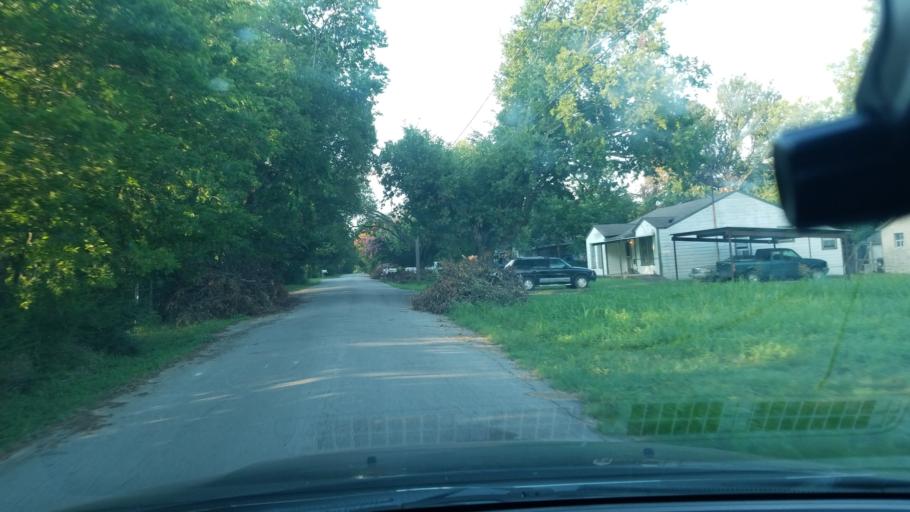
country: US
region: Texas
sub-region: Dallas County
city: Balch Springs
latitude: 32.7231
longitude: -96.6649
